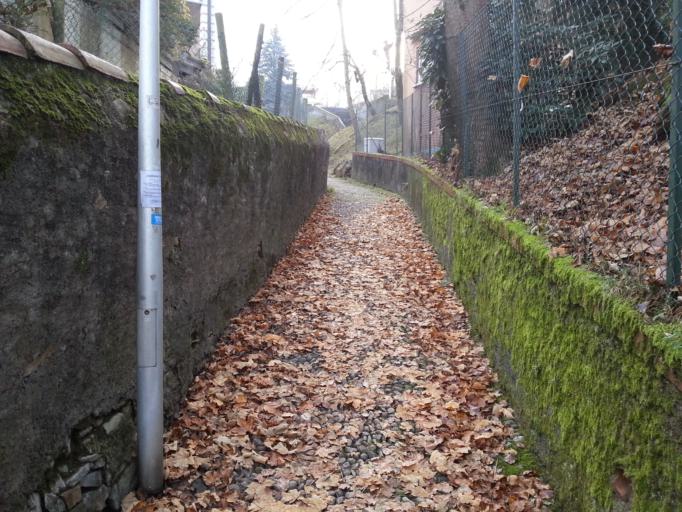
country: CH
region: Ticino
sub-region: Mendrisio District
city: Mendrisio
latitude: 45.8635
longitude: 8.9830
